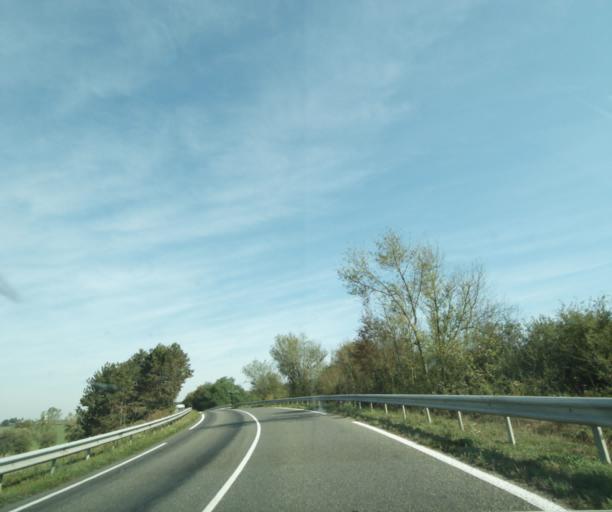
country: FR
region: Bourgogne
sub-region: Departement de Saone-et-Loire
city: Genelard
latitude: 46.5918
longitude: 4.2317
